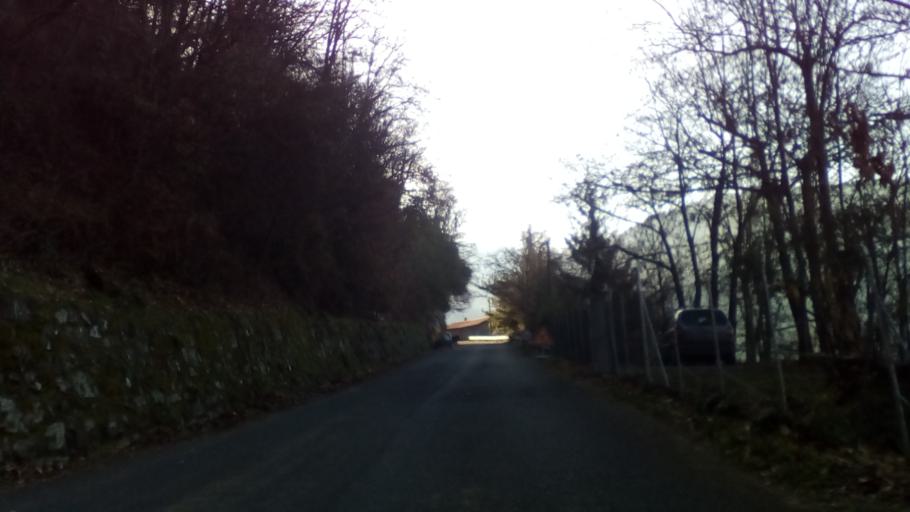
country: IT
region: Tuscany
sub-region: Provincia di Massa-Carrara
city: Montignoso
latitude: 44.0587
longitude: 10.1850
